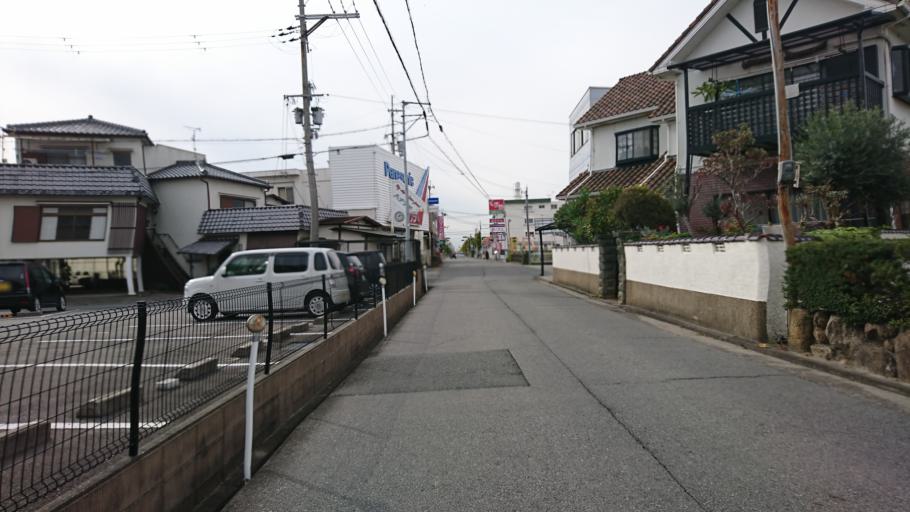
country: JP
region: Hyogo
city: Kakogawacho-honmachi
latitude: 34.7896
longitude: 134.8787
